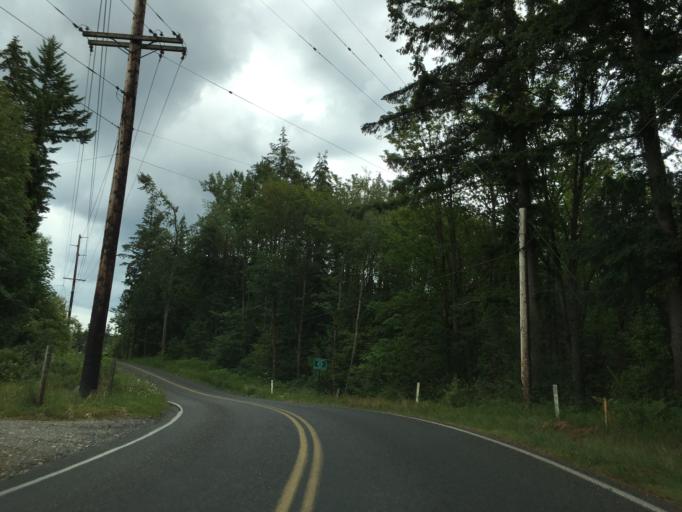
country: US
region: Washington
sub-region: Whatcom County
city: Geneva
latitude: 48.7898
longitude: -122.4290
